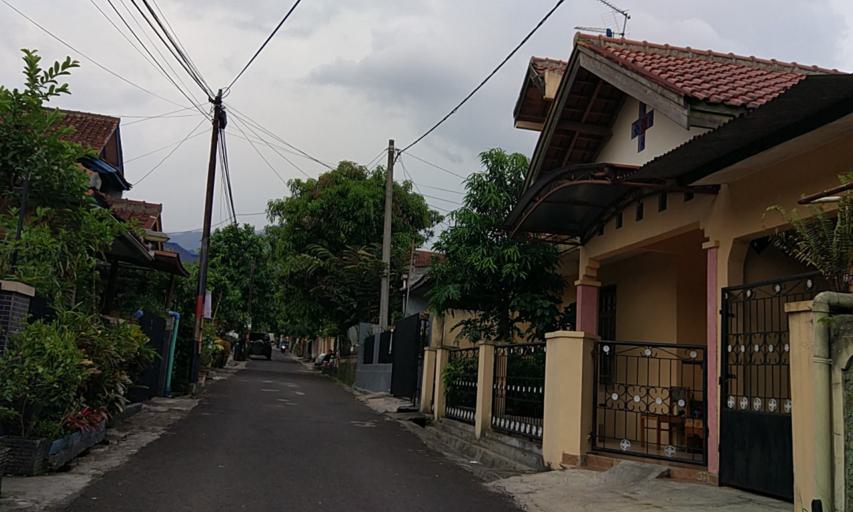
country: ID
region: West Java
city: Cileunyi
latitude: -6.9047
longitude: 107.6921
